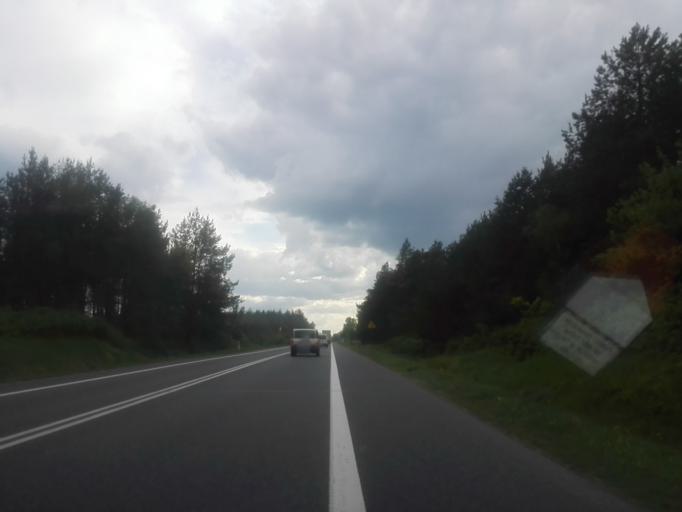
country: PL
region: Podlasie
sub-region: Powiat zambrowski
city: Szumowo
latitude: 52.8625
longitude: 22.0051
